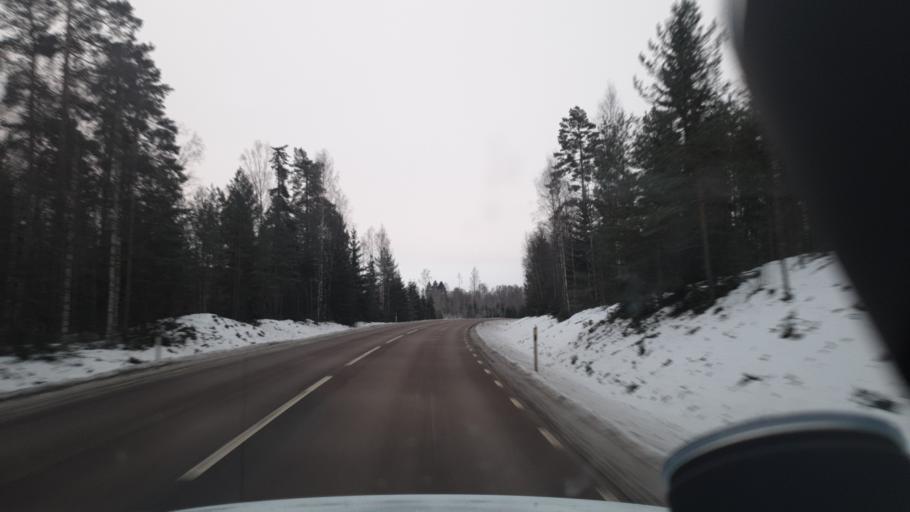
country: SE
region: Vaermland
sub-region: Eda Kommun
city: Charlottenberg
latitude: 59.8401
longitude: 12.3172
